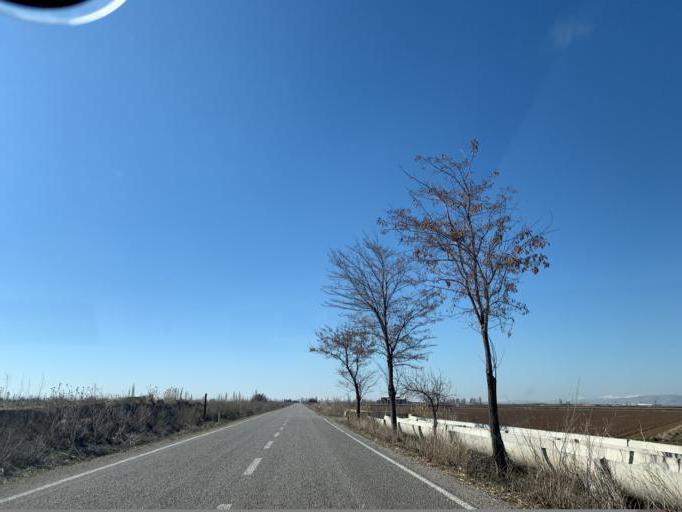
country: TR
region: Konya
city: Cumra
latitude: 37.6191
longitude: 32.8005
